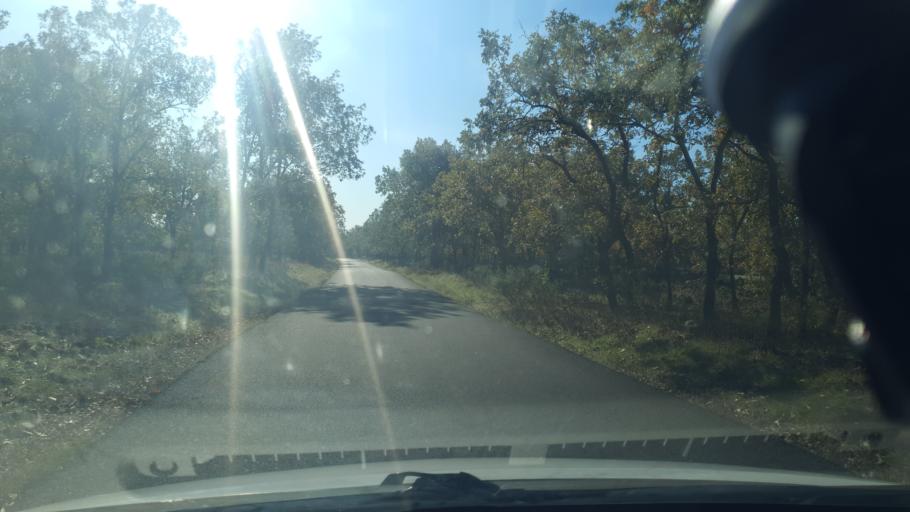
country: ES
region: Castille and Leon
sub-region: Provincia de Avila
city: Candeleda
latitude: 40.1258
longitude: -5.2670
